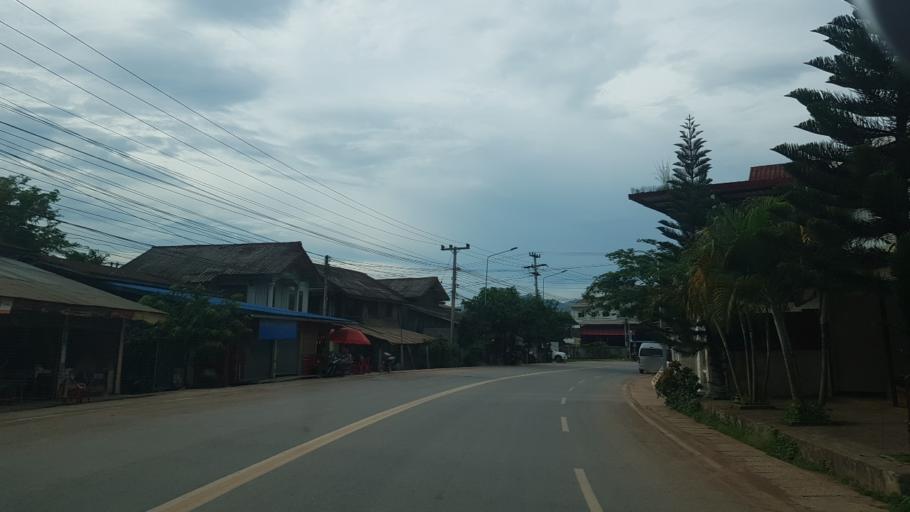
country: LA
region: Oudomxai
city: Muang Xay
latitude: 20.6615
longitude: 101.9758
